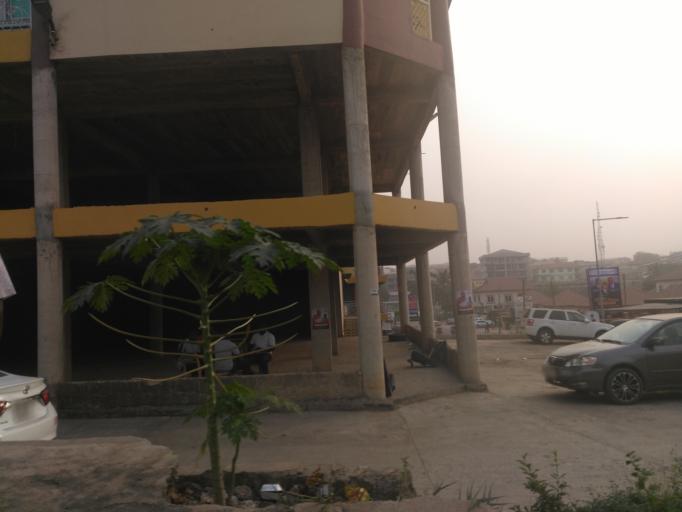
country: GH
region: Ashanti
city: Kumasi
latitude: 6.7104
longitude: -1.6165
